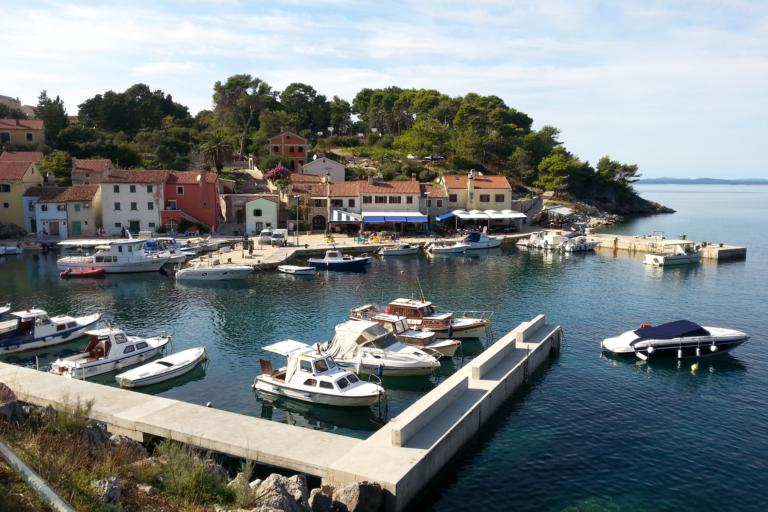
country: HR
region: Primorsko-Goranska
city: Mali Losinj
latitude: 44.5198
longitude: 14.5071
